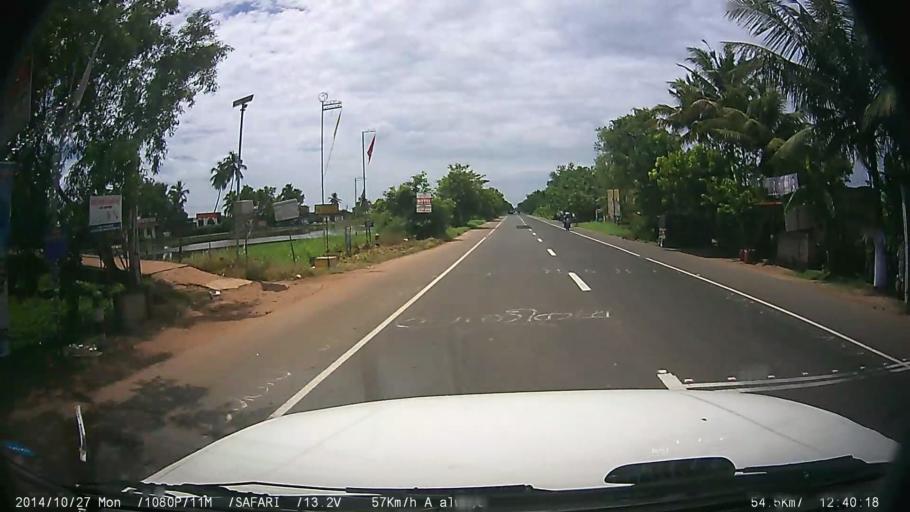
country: IN
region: Kerala
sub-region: Kottayam
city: Changanacheri
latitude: 9.4309
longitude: 76.5244
